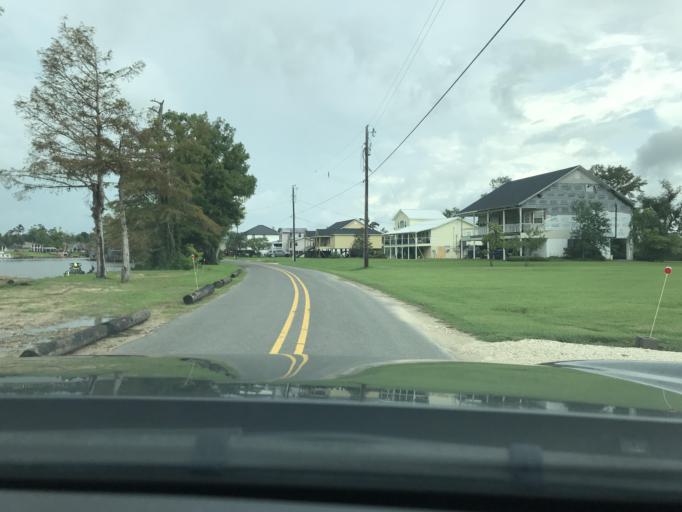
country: US
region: Louisiana
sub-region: Calcasieu Parish
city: Moss Bluff
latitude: 30.2757
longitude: -93.2230
